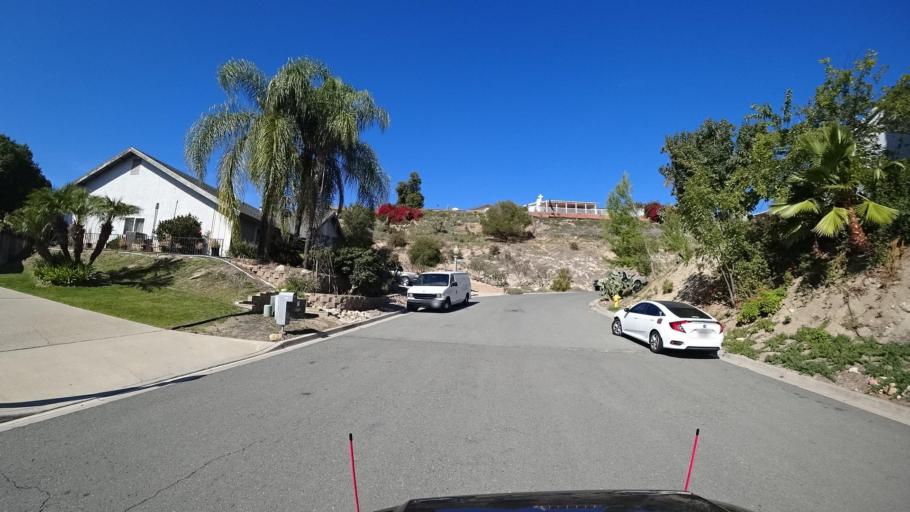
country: US
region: California
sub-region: San Diego County
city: Casa de Oro-Mount Helix
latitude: 32.7566
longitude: -116.9825
